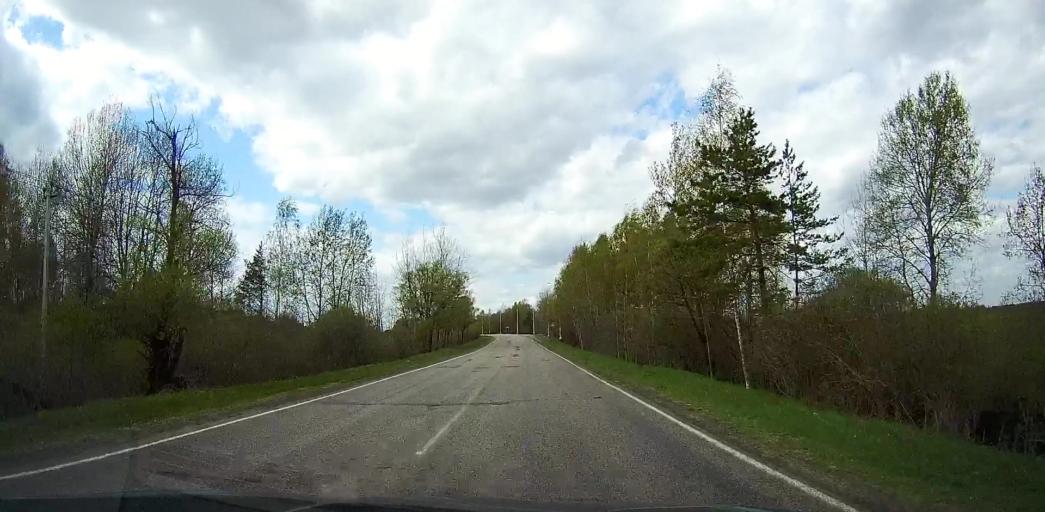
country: RU
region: Moskovskaya
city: Davydovo
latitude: 55.6626
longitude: 38.8066
